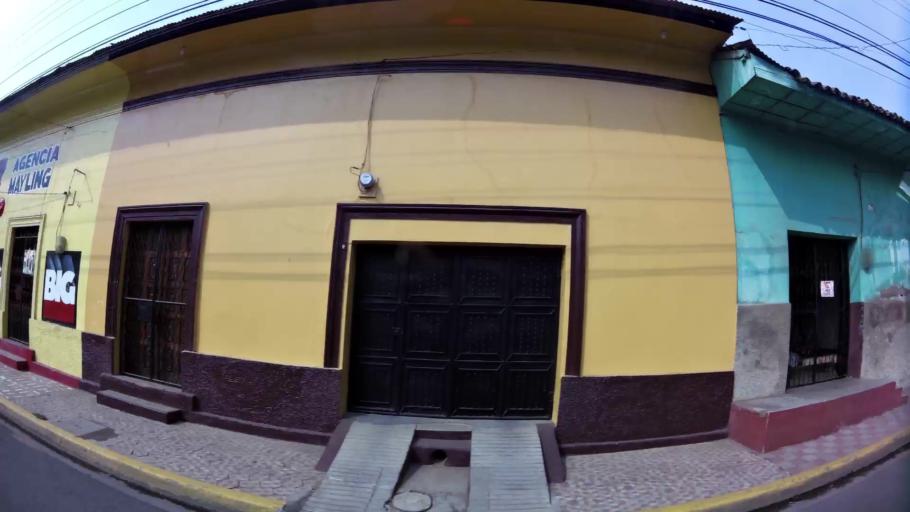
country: NI
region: Masaya
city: Masaya
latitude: 11.9754
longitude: -86.0977
